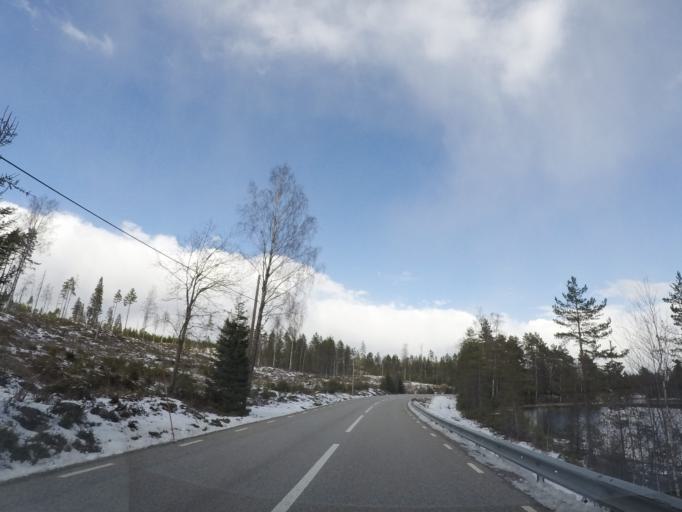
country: SE
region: OErebro
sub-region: Lindesbergs Kommun
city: Stora
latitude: 59.8933
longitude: 15.2604
